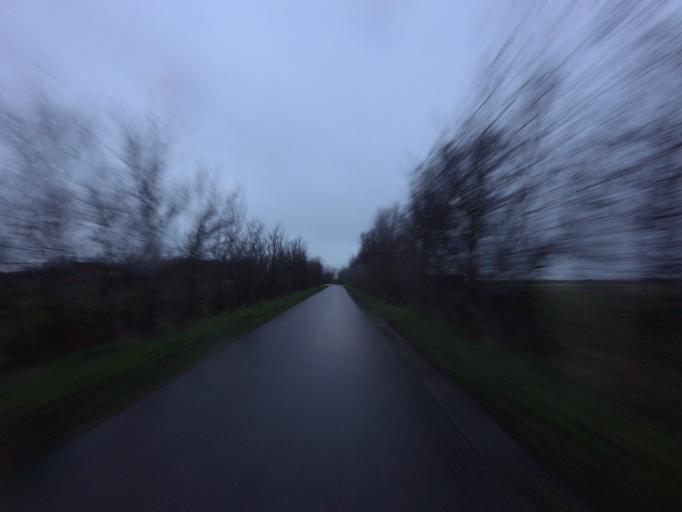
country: NL
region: North Holland
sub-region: Gemeente Texel
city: Den Burg
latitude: 53.0670
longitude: 4.7962
